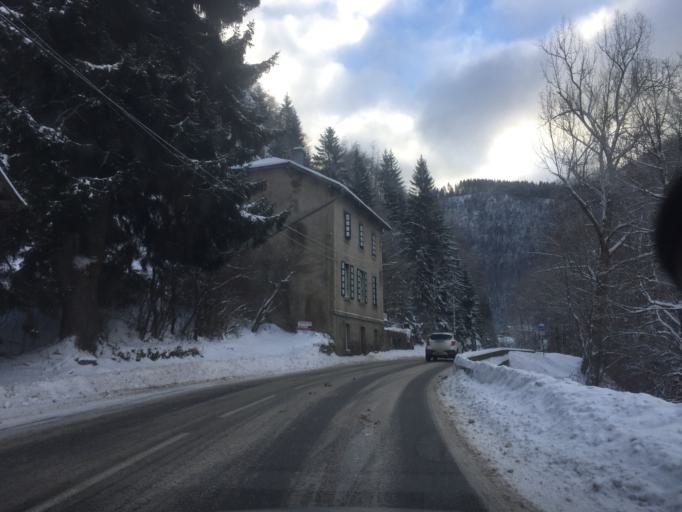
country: FR
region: Rhone-Alpes
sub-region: Departement de la Haute-Savoie
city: Abondance
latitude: 46.2876
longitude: 6.6950
